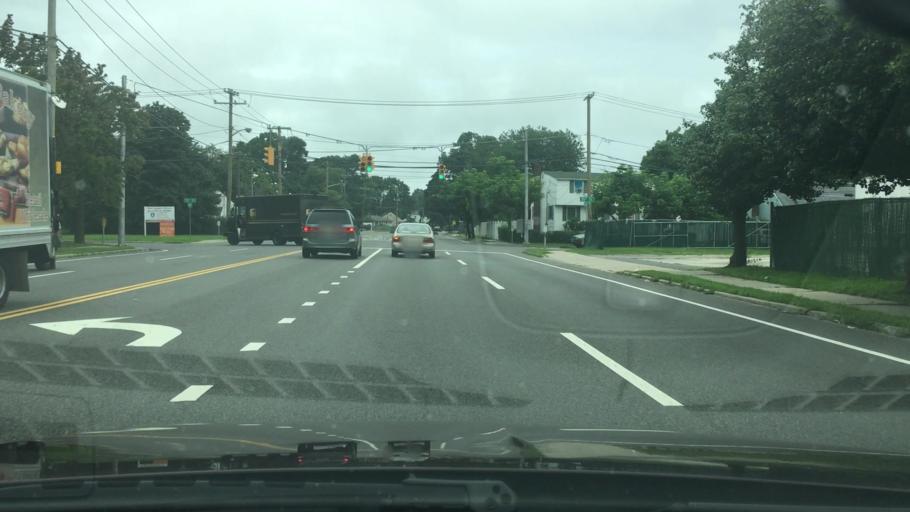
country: US
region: New York
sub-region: Suffolk County
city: Copiague
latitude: 40.6924
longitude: -73.3935
